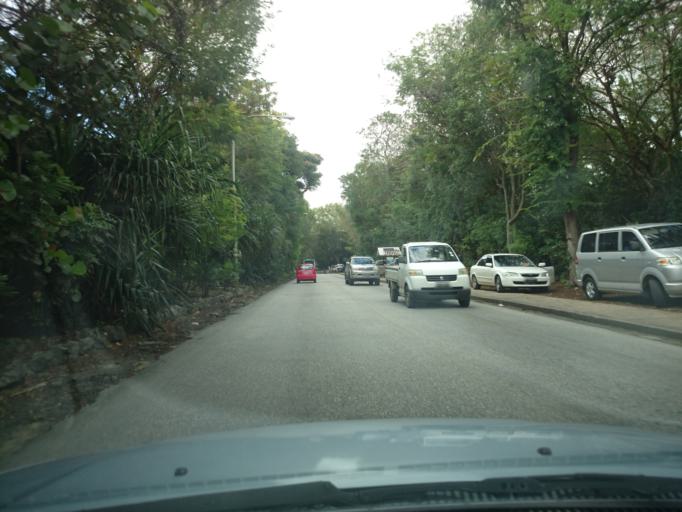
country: BB
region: Saint James
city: Holetown
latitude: 13.1710
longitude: -59.6367
